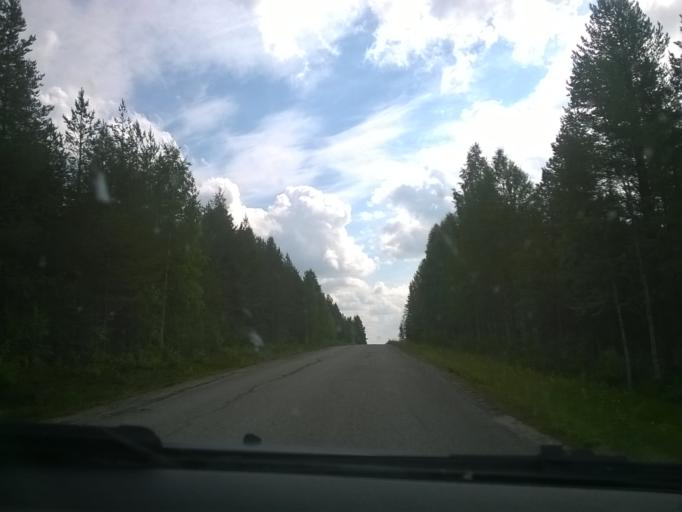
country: FI
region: Kainuu
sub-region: Kehys-Kainuu
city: Kuhmo
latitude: 64.4328
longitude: 29.7174
